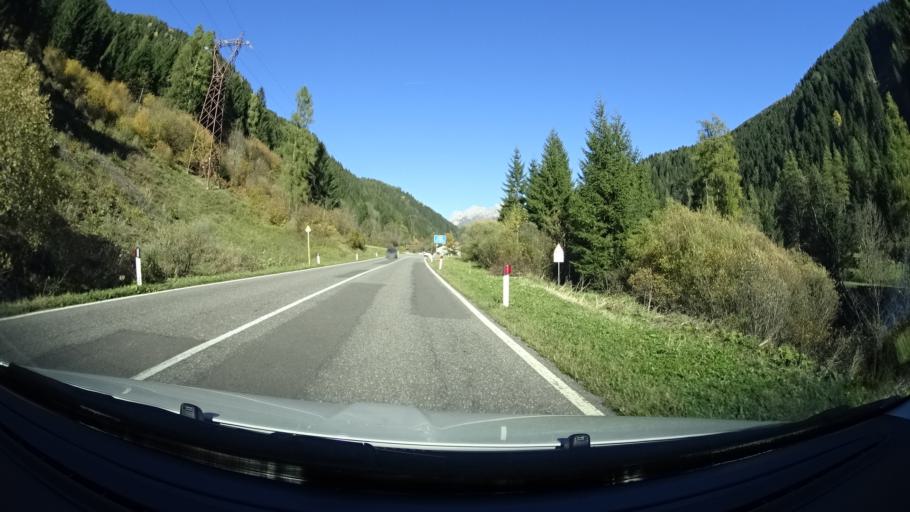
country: IT
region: Trentino-Alto Adige
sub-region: Provincia di Trento
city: Predazzo
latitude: 46.3350
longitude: 11.6054
